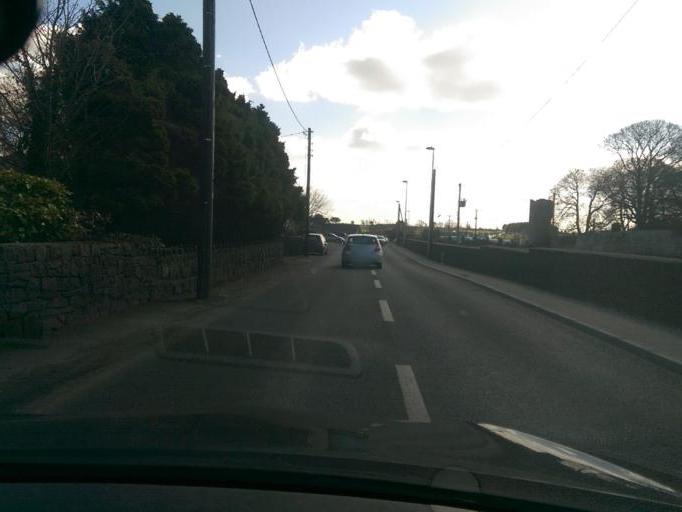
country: IE
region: Connaught
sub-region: County Galway
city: Athenry
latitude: 53.2971
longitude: -8.7429
